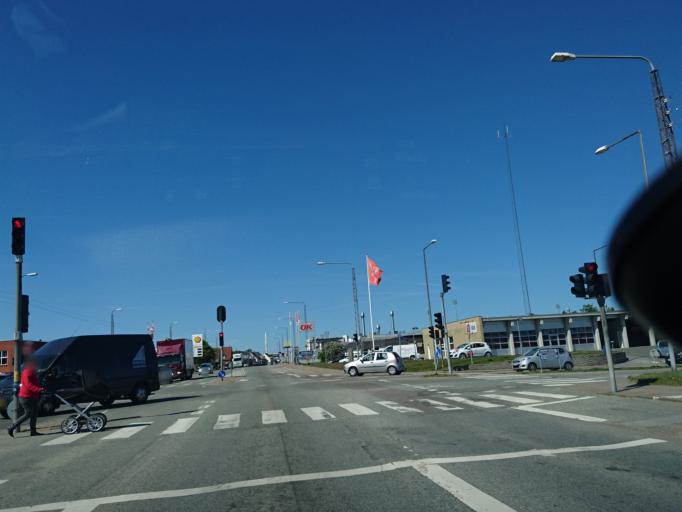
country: DK
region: North Denmark
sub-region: Hjorring Kommune
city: Hjorring
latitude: 57.4558
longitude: 10.0062
